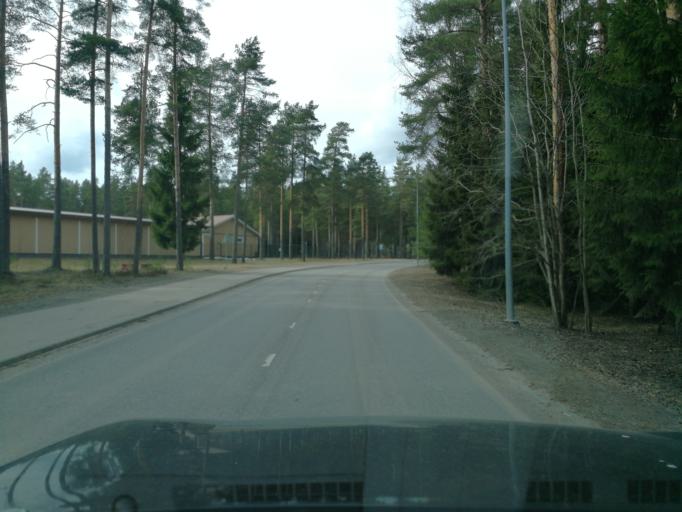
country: FI
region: Uusimaa
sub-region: Helsinki
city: Lohja
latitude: 60.2383
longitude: 24.0695
